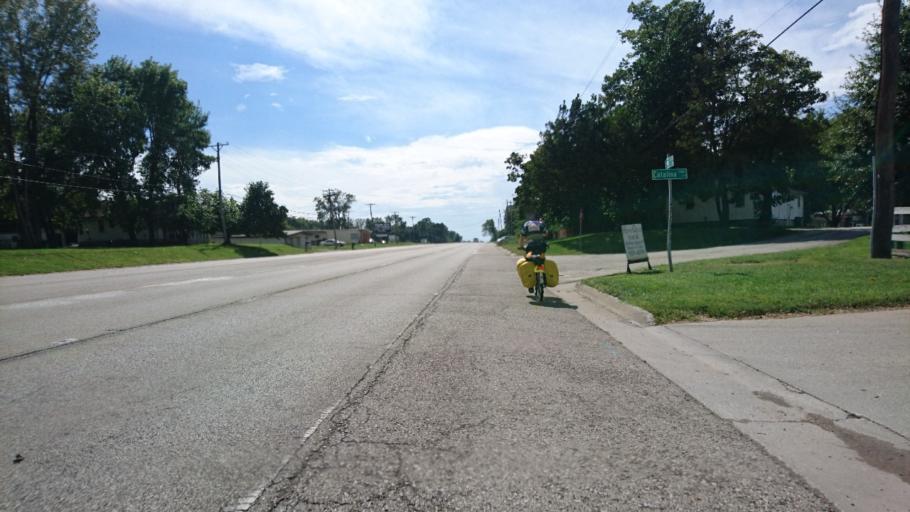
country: US
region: Illinois
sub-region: Sangamon County
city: Grandview
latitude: 39.8532
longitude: -89.6214
